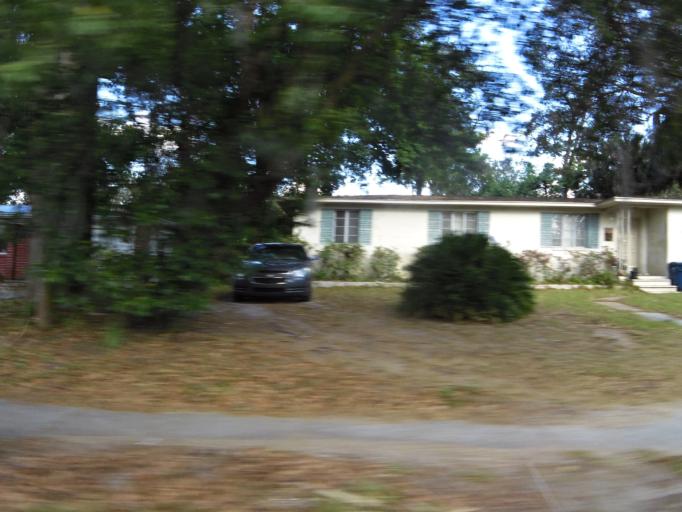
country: US
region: Florida
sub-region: Duval County
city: Jacksonville
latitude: 30.3386
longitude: -81.5972
